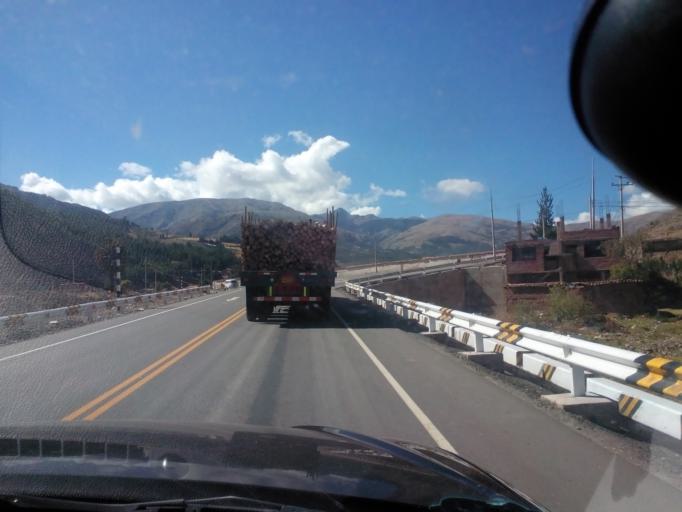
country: PE
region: Cusco
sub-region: Provincia de Quispicanchis
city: Urcos
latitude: -13.6842
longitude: -71.6219
